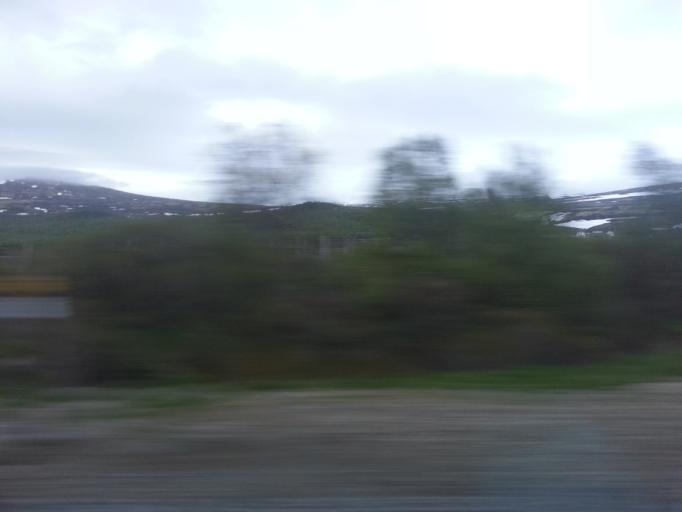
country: NO
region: Oppland
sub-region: Dovre
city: Dovre
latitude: 62.1201
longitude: 9.2777
